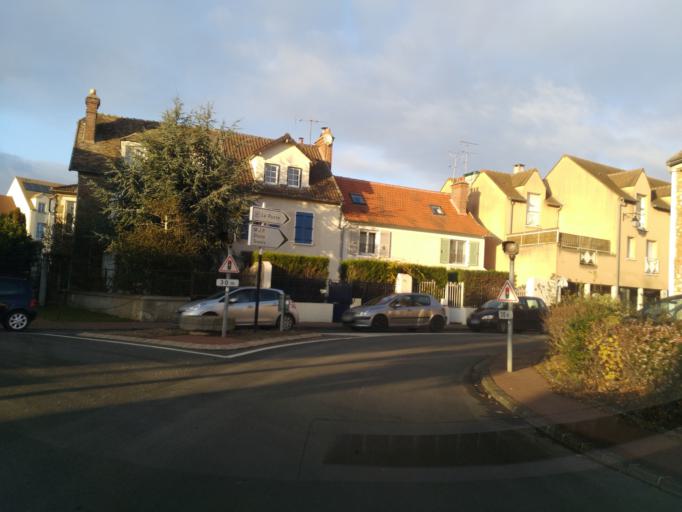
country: FR
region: Ile-de-France
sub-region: Departement des Yvelines
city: Neauphle-le-Chateau
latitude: 48.8142
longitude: 1.9034
